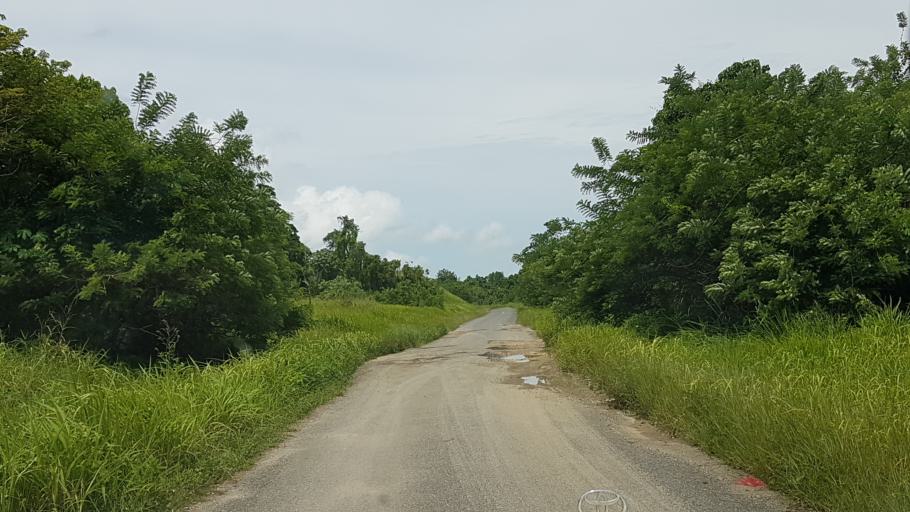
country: PG
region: Madang
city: Madang
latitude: -4.5736
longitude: 145.5125
